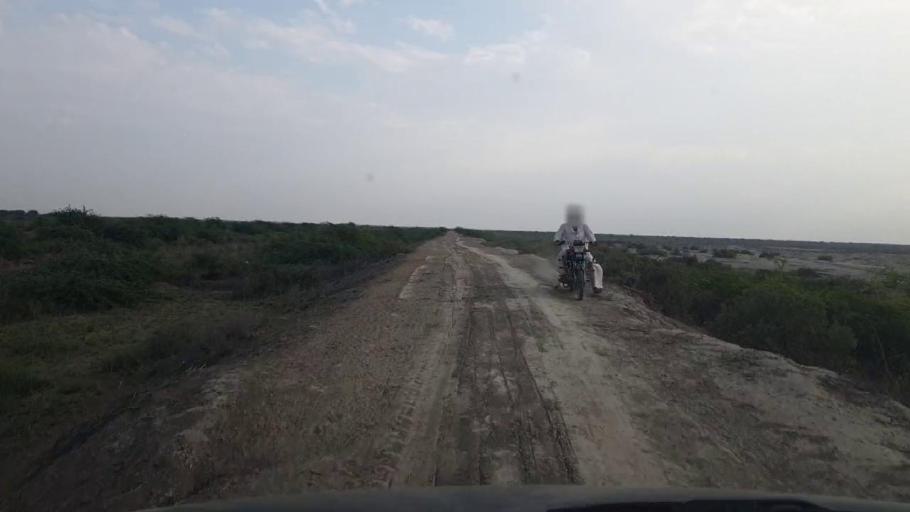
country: PK
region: Sindh
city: Badin
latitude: 24.4813
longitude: 68.6984
